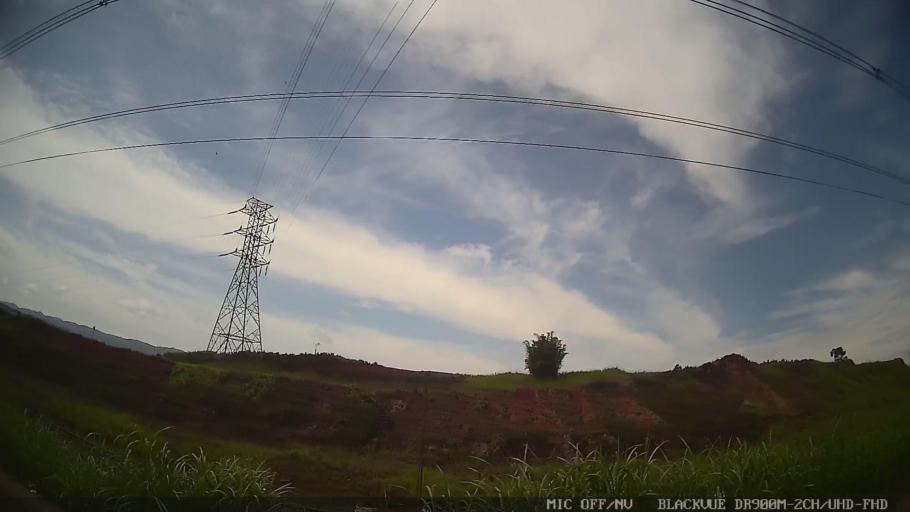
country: BR
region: Sao Paulo
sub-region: Aruja
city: Aruja
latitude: -23.4337
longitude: -46.2639
